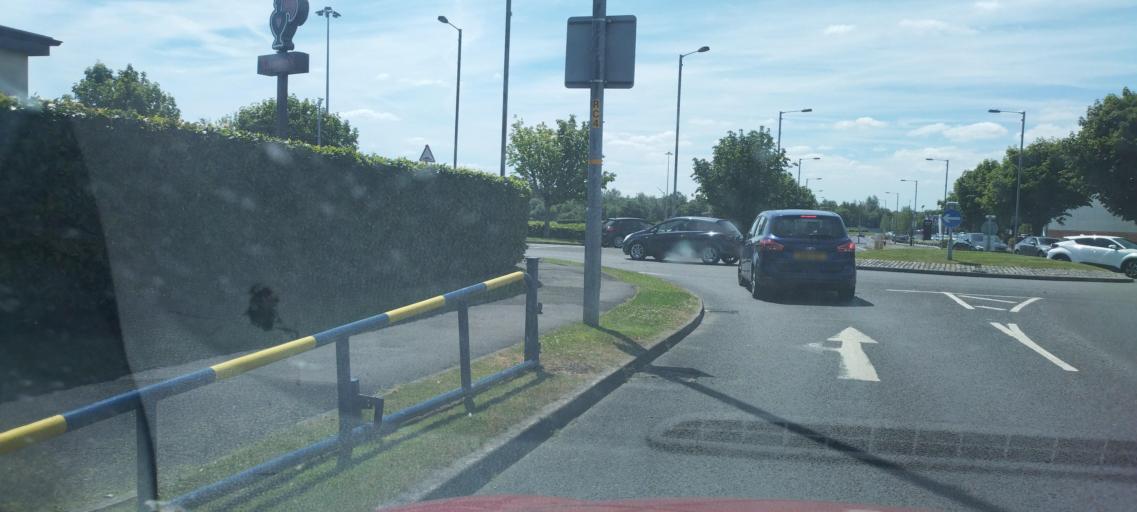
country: GB
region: England
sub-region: Borough of Bolton
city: Horwich
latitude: 53.5842
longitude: -2.5380
